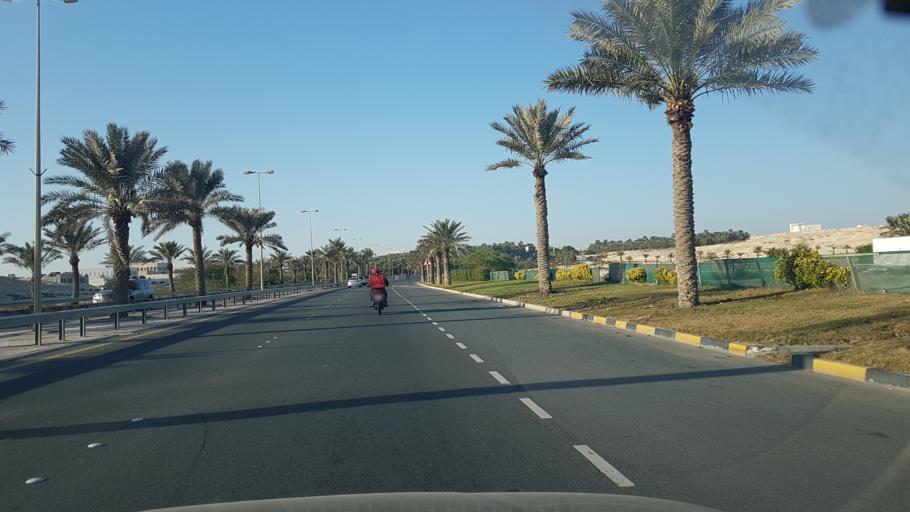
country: BH
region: Northern
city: Ar Rifa'
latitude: 26.1108
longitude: 50.5384
